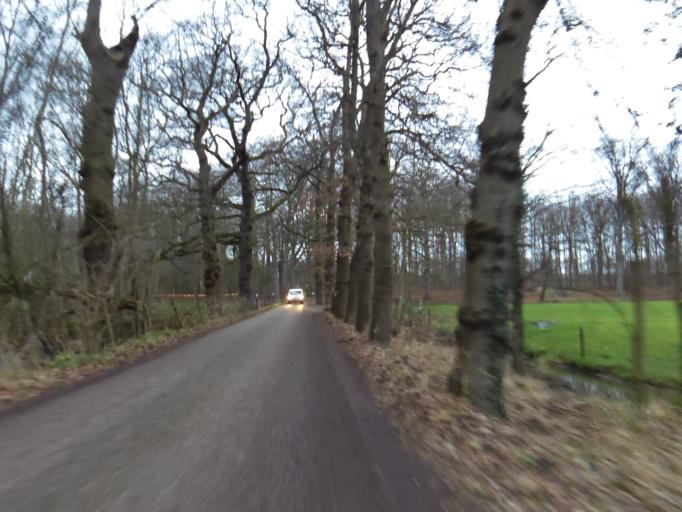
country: NL
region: North Holland
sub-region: Gemeente Bloemendaal
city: Bennebroek
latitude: 52.3306
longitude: 4.5688
